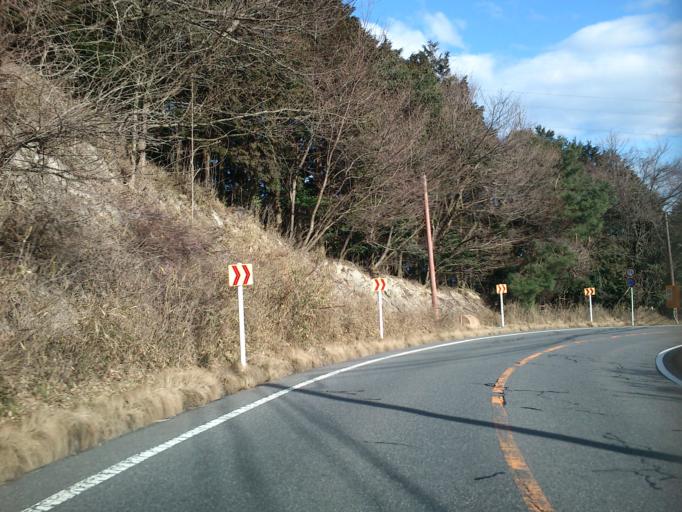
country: JP
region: Shiga Prefecture
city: Otsu-shi
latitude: 35.0343
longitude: 135.8393
